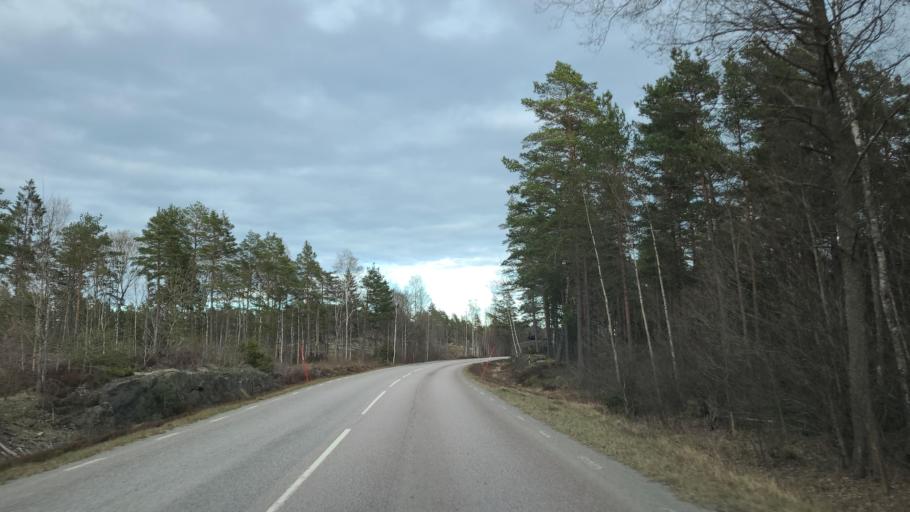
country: SE
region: OEstergoetland
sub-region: Norrkopings Kommun
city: Krokek
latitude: 58.6507
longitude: 16.5556
